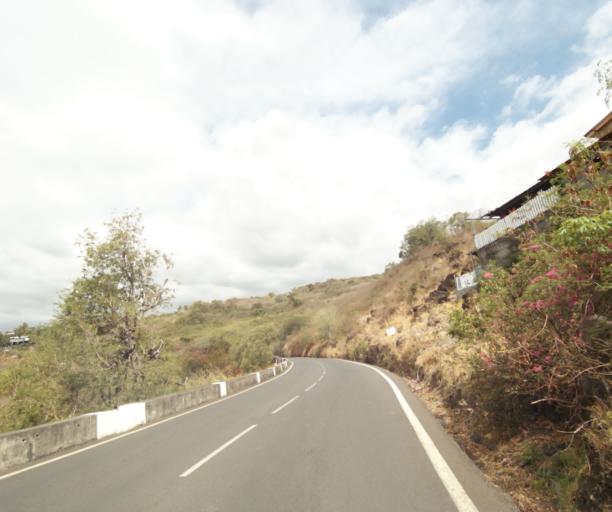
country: RE
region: Reunion
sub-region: Reunion
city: Saint-Paul
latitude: -21.0155
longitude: 55.2810
